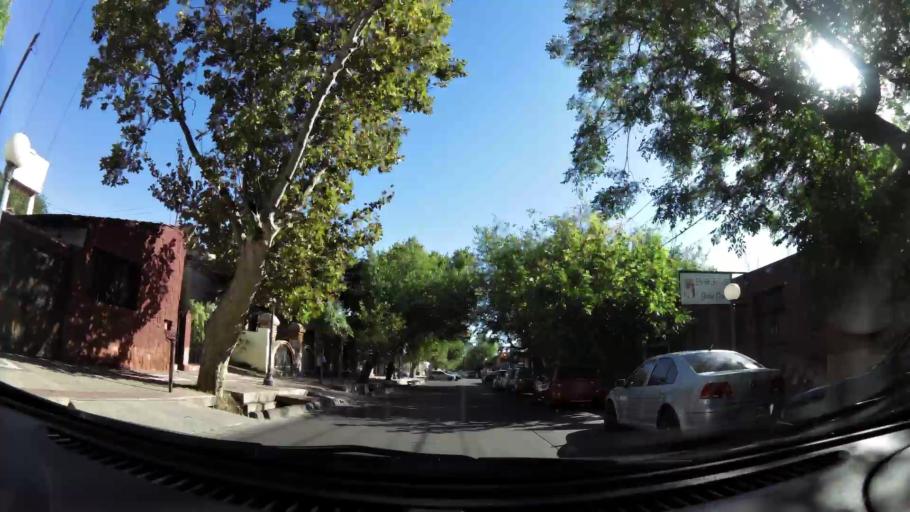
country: AR
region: Mendoza
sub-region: Departamento de Godoy Cruz
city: Godoy Cruz
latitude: -32.9236
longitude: -68.8433
